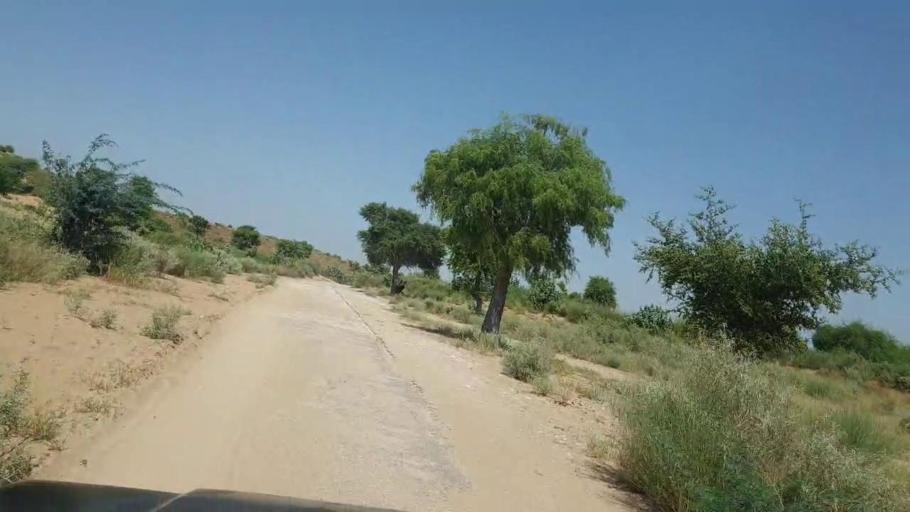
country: PK
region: Sindh
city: Chor
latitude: 25.3930
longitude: 70.3134
